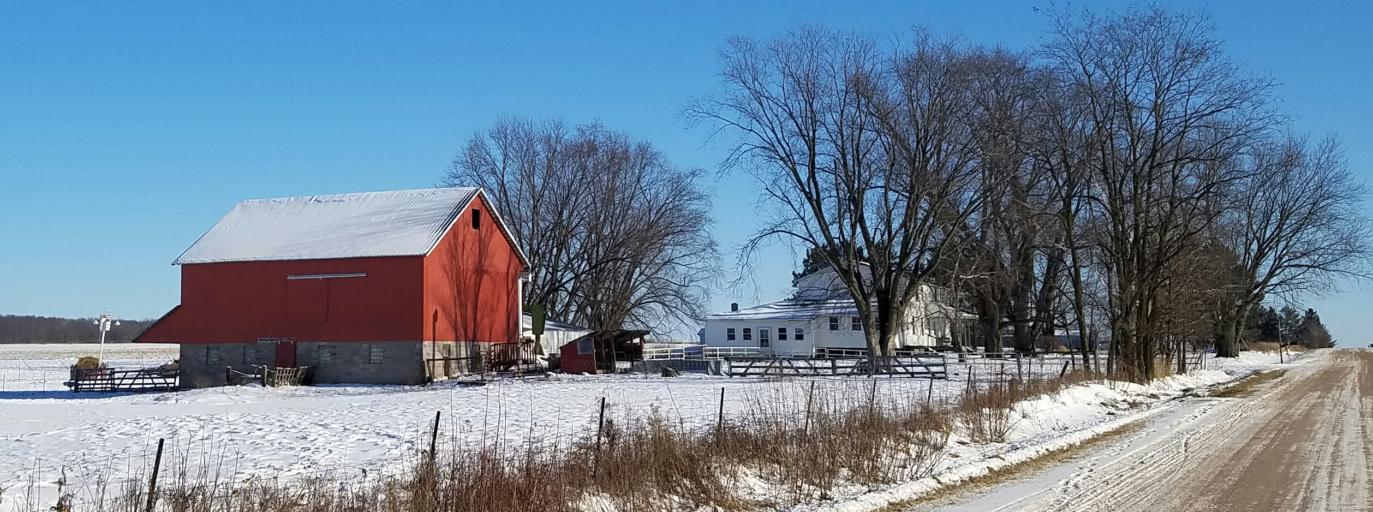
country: US
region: Wisconsin
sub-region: Clark County
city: Neillsville
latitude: 44.5675
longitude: -90.4409
